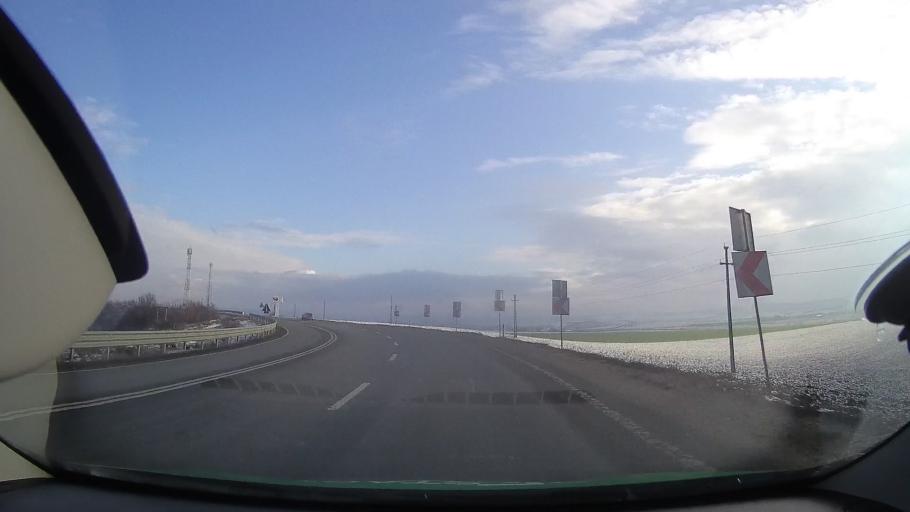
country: RO
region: Mures
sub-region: Comuna Iernut
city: Iernut
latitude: 46.4501
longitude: 24.2082
